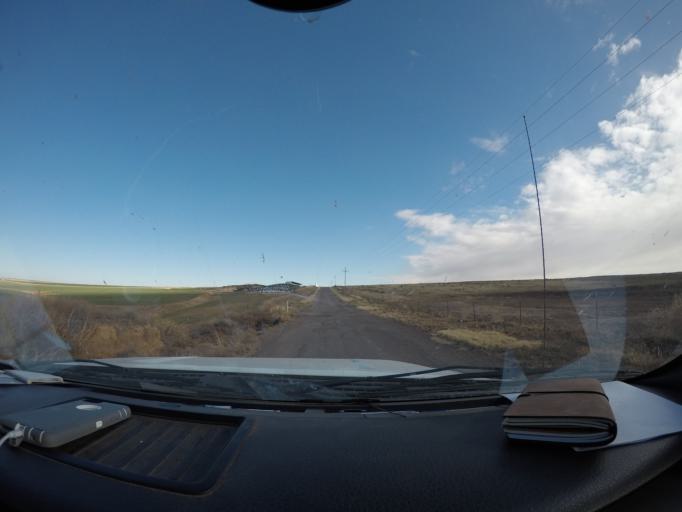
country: US
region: Texas
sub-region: Parmer County
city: Bovina
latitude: 34.6326
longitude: -103.0867
